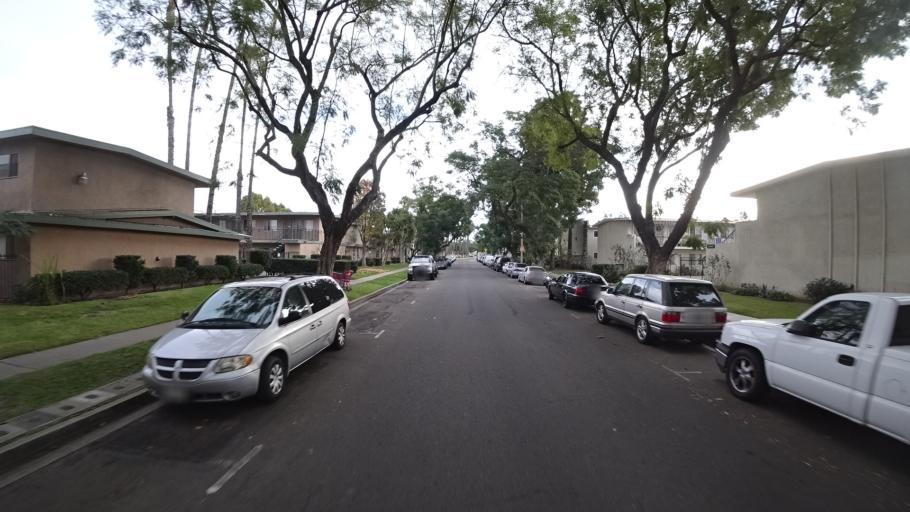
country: US
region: California
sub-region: Orange County
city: Garden Grove
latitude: 33.7731
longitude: -117.9267
